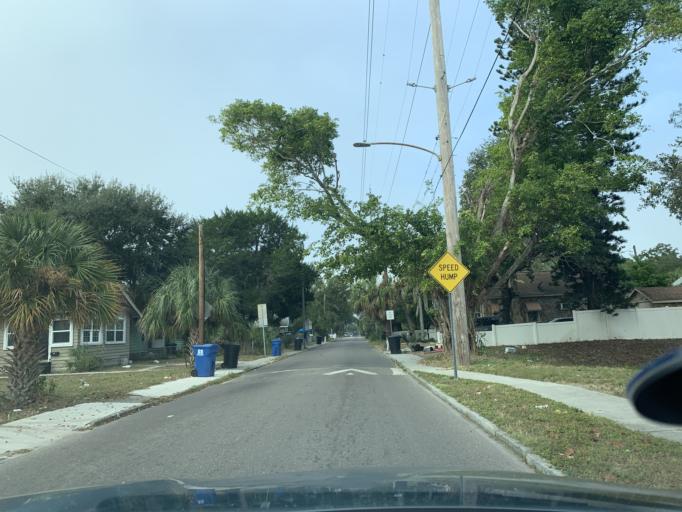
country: US
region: Florida
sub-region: Pinellas County
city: Saint Petersburg
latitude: 27.7594
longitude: -82.6473
